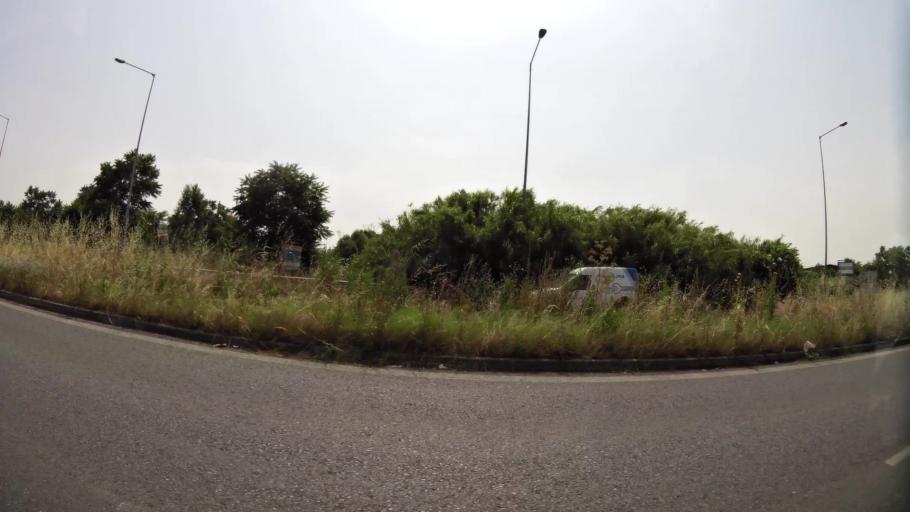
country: GR
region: Central Macedonia
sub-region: Nomos Thessalonikis
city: Nea Magnisia
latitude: 40.6917
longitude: 22.8475
